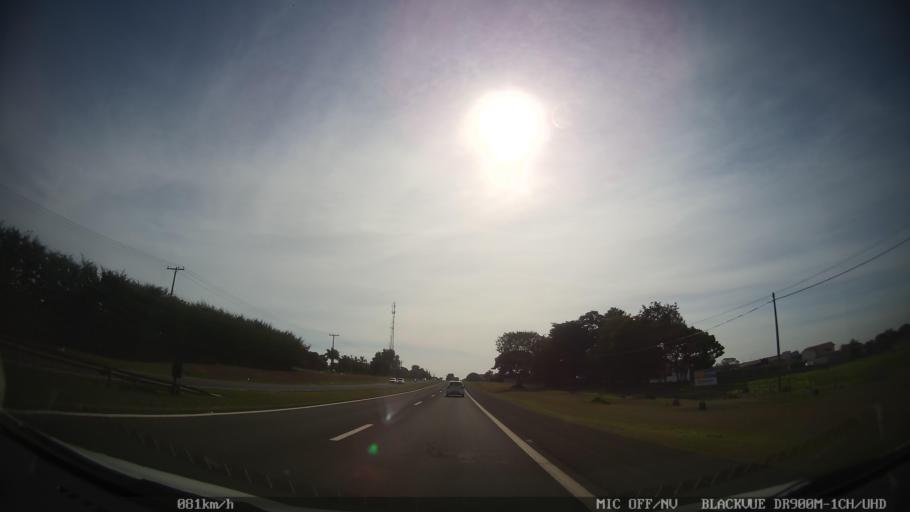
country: BR
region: Sao Paulo
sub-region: Piracicaba
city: Piracicaba
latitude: -22.7697
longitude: -47.6474
